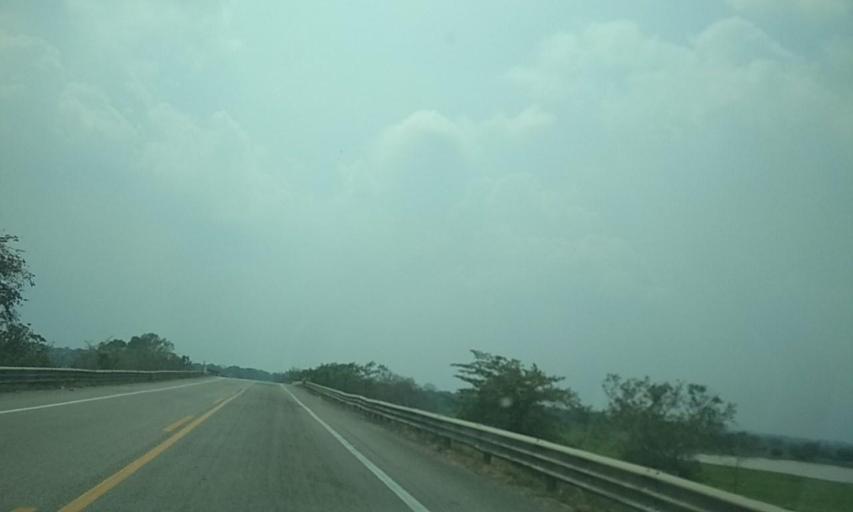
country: MX
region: Tabasco
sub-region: Huimanguillo
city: Francisco Rueda
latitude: 17.7685
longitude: -94.0340
